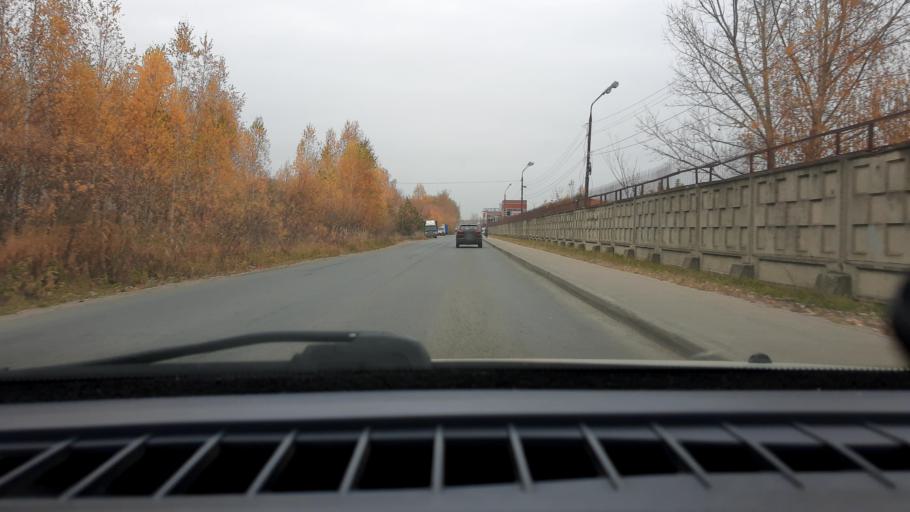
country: RU
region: Nizjnij Novgorod
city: Gorbatovka
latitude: 56.3329
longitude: 43.8065
